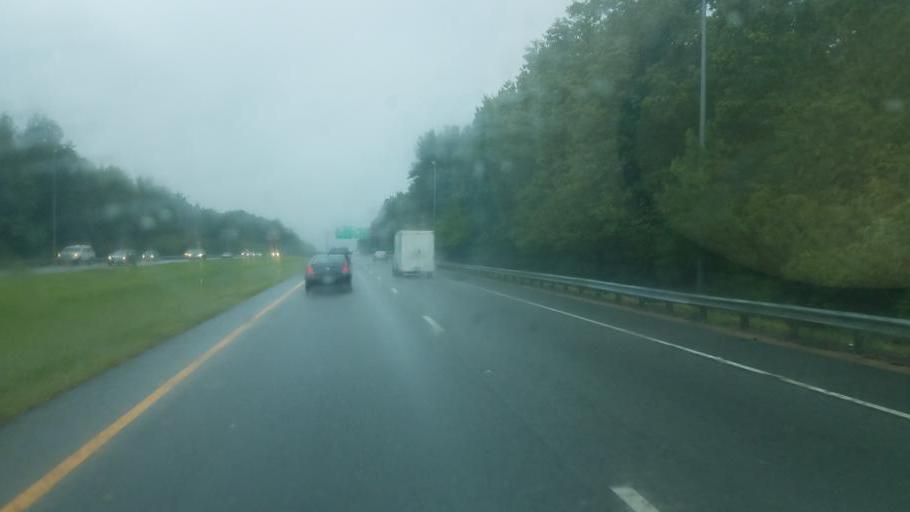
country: US
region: Virginia
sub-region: City of Portsmouth
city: Portsmouth Heights
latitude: 36.7596
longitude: -76.3302
